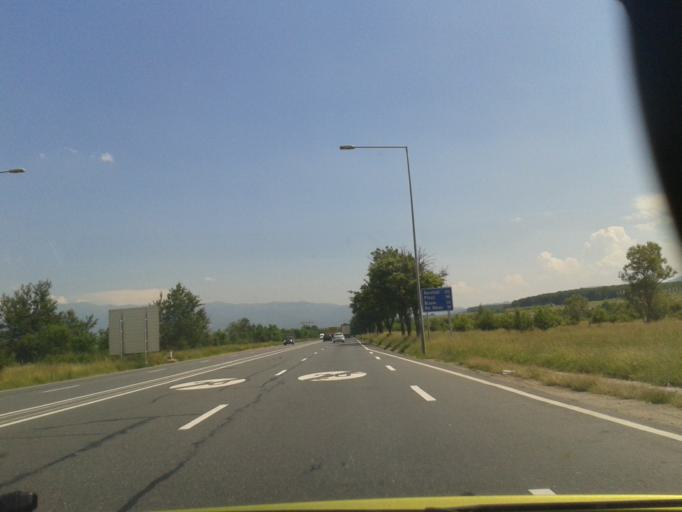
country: RO
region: Sibiu
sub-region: Comuna Selimbar
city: Selimbar
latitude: 45.7427
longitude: 24.2055
